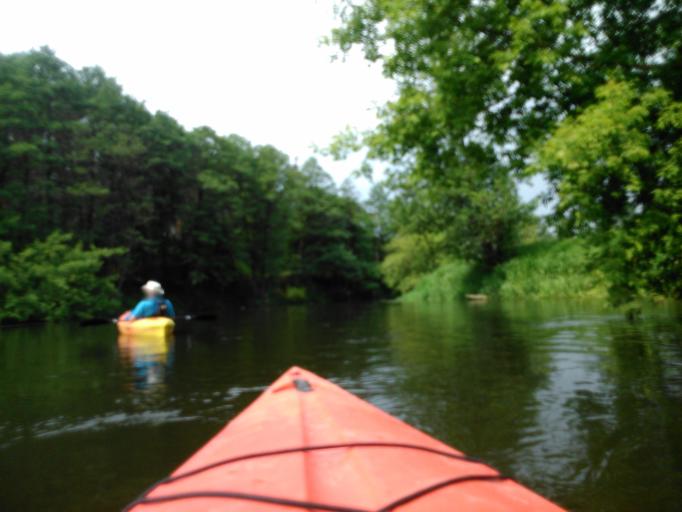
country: PL
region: Kujawsko-Pomorskie
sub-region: Powiat golubsko-dobrzynski
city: Golub-Dobrzyn
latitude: 53.1047
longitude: 19.0317
